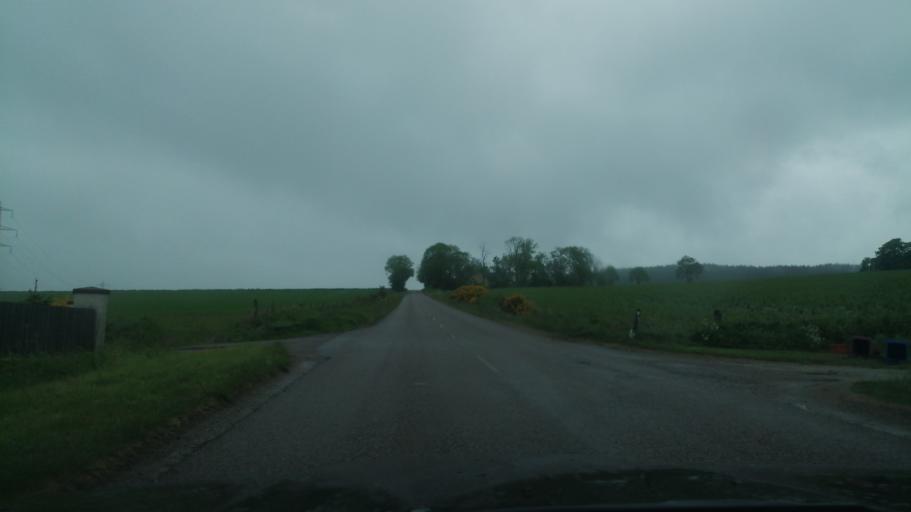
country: GB
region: Scotland
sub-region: Aberdeenshire
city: Huntly
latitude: 57.5452
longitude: -2.8099
